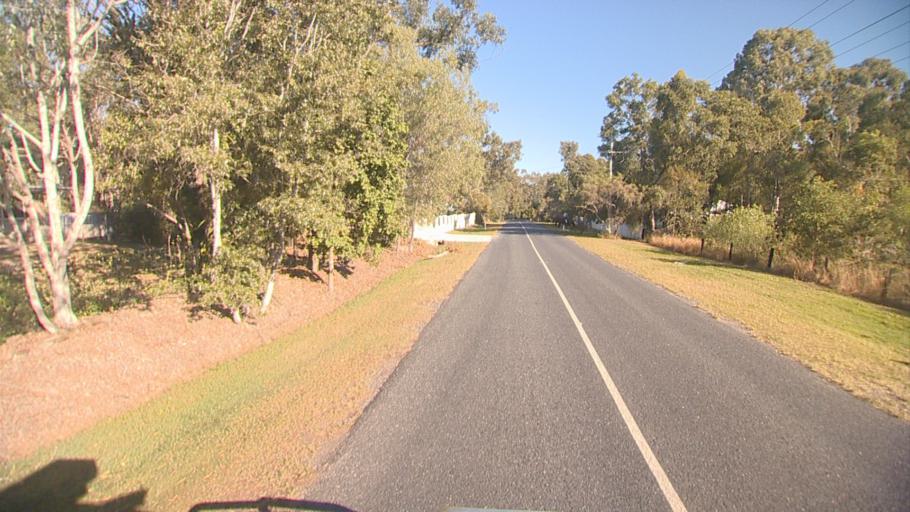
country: AU
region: Queensland
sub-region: Logan
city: Logan Reserve
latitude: -27.7389
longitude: 153.1030
